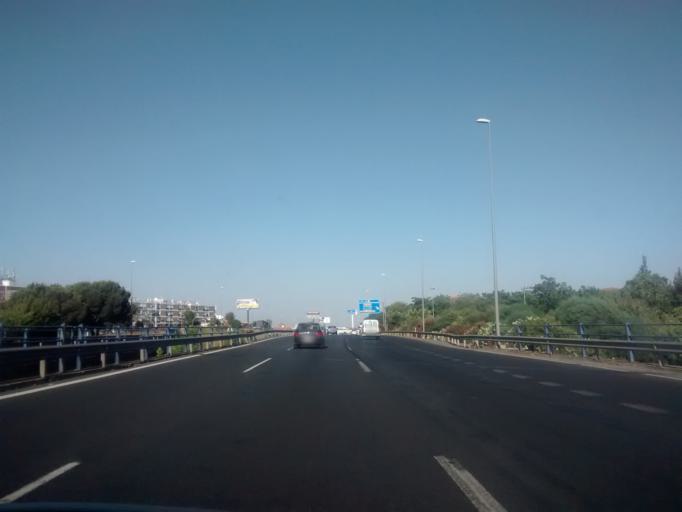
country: ES
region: Andalusia
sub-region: Provincia de Sevilla
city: Castilleja de la Cuesta
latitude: 37.3834
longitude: -6.0616
